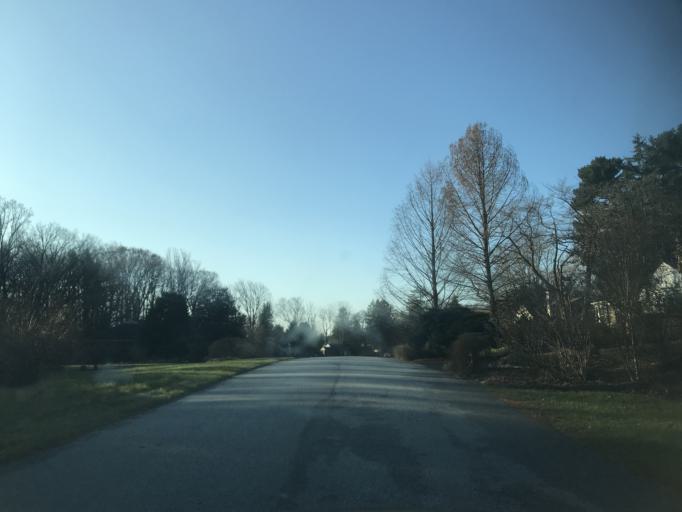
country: US
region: Maryland
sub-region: Baltimore County
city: Towson
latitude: 39.3902
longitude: -76.5845
